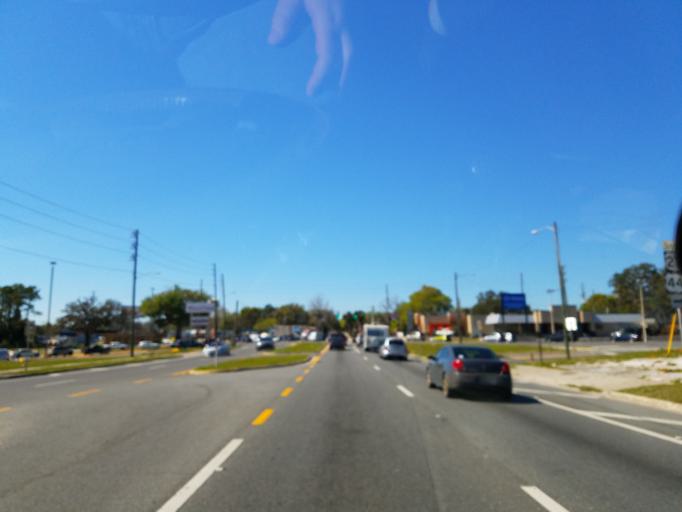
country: US
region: Florida
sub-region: Marion County
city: Belleview
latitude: 29.0573
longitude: -82.0491
